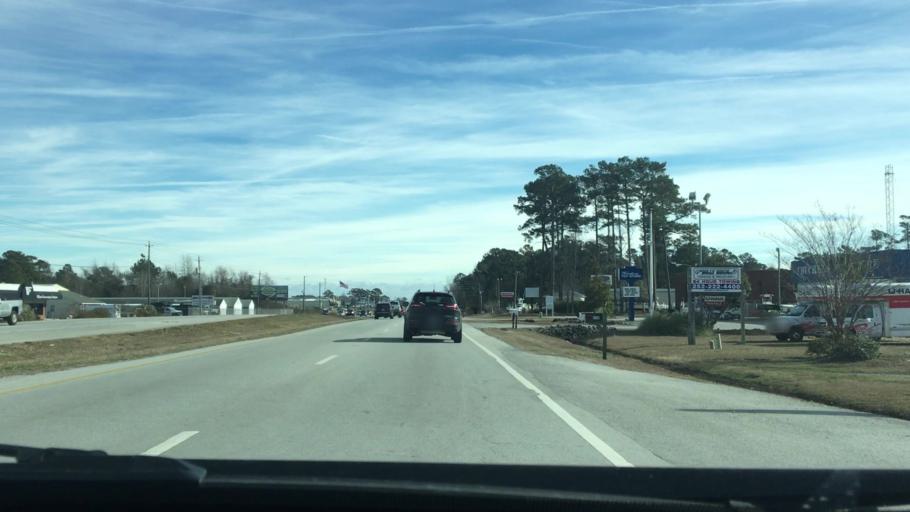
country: US
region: North Carolina
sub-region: Carteret County
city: Pine Knoll Shores
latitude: 34.7449
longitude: -76.8298
